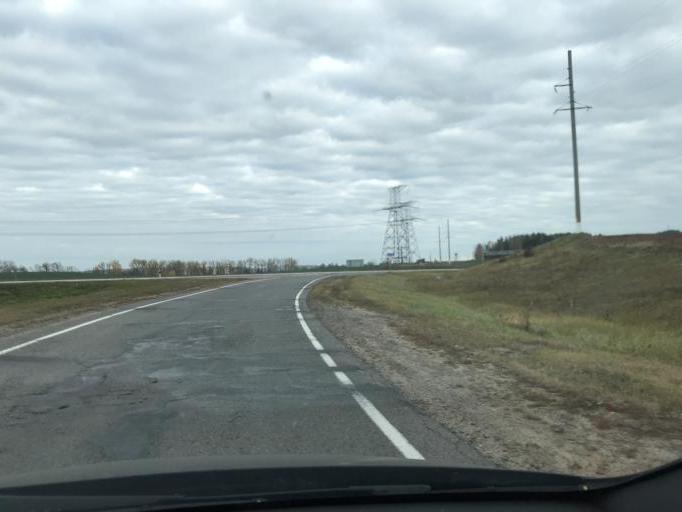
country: BY
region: Minsk
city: Astrashytski Haradok
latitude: 54.0560
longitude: 27.7064
